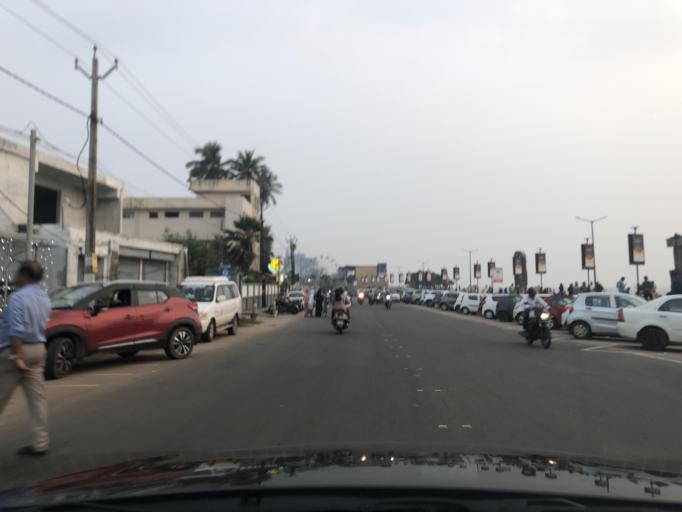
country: IN
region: Kerala
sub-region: Kozhikode
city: Kozhikode
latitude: 11.2523
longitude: 75.7710
